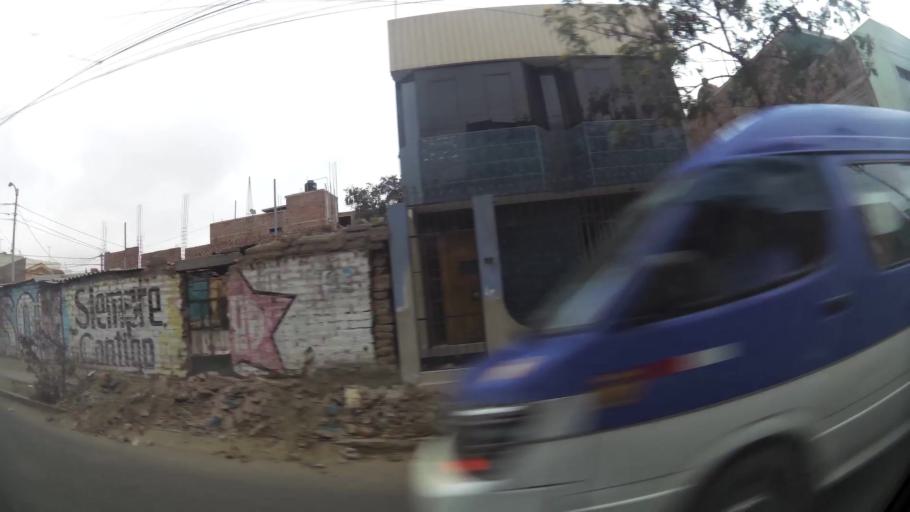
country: PE
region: La Libertad
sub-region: Provincia de Trujillo
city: El Porvenir
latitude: -8.0804
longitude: -79.0196
